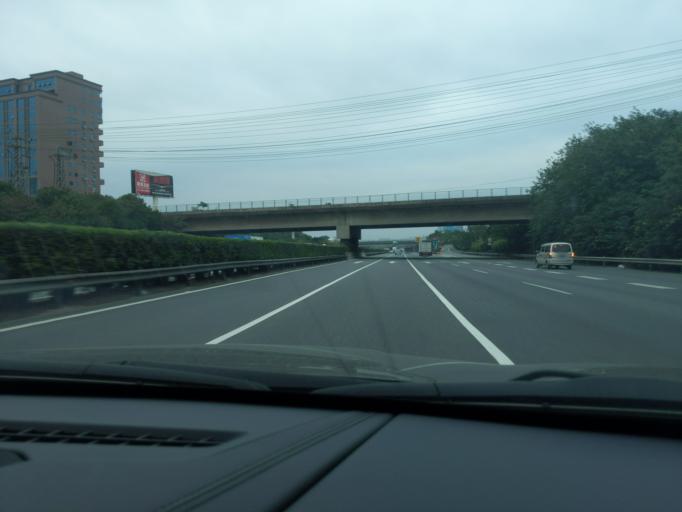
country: CN
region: Fujian
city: Anhai
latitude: 24.7272
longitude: 118.4119
